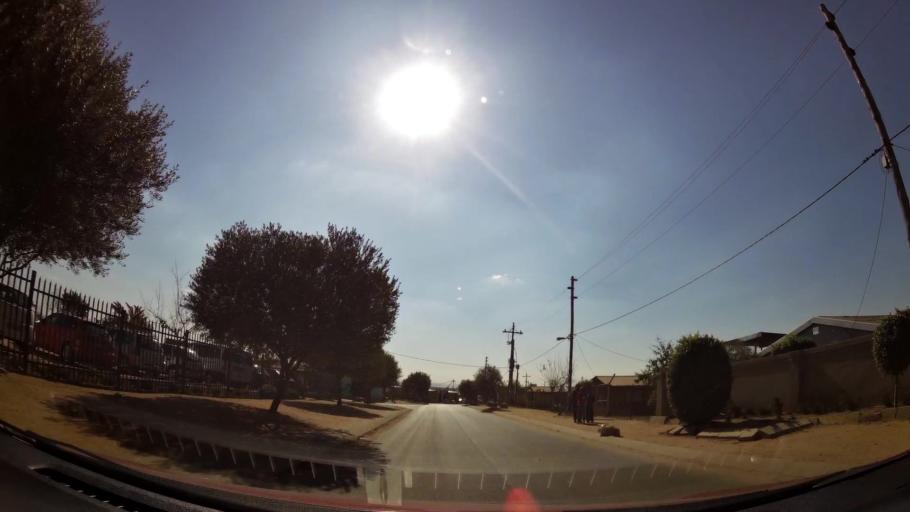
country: ZA
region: Gauteng
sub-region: West Rand District Municipality
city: Muldersdriseloop
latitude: -26.0280
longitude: 27.9262
